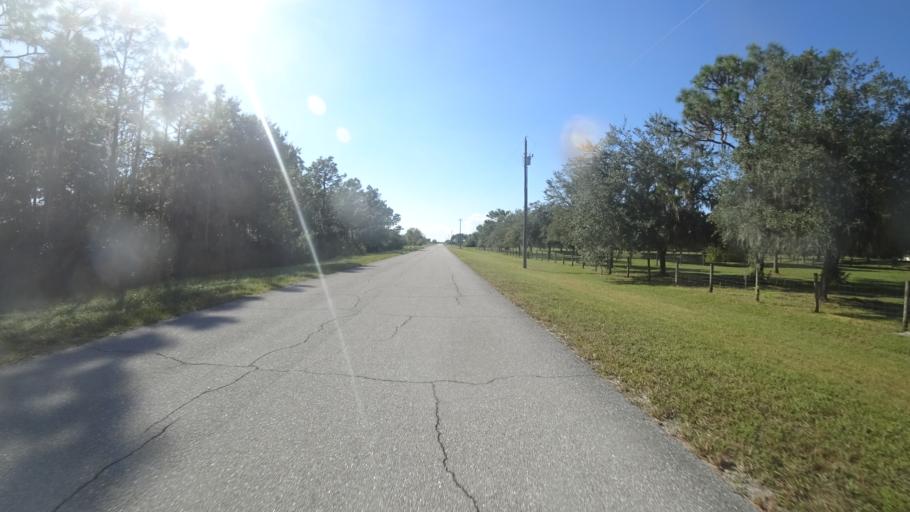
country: US
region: Florida
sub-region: Sarasota County
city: The Meadows
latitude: 27.4232
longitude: -82.2734
